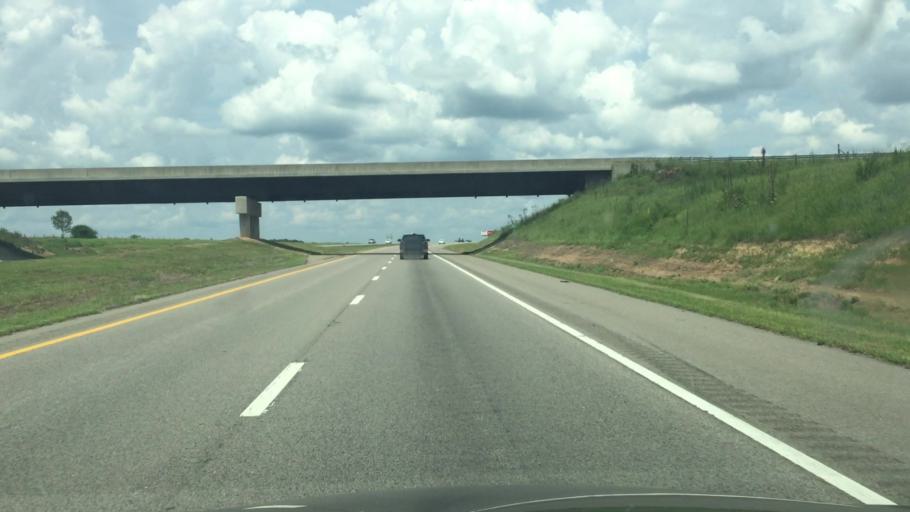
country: US
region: North Carolina
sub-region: Richmond County
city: Ellerbe
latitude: 35.1865
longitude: -79.7211
